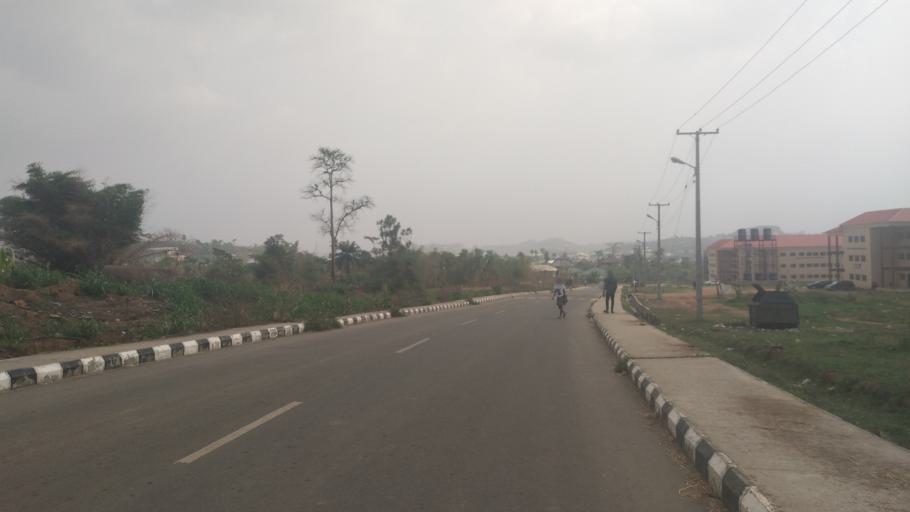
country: NG
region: Ondo
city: Ilare
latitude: 7.2972
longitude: 5.1356
